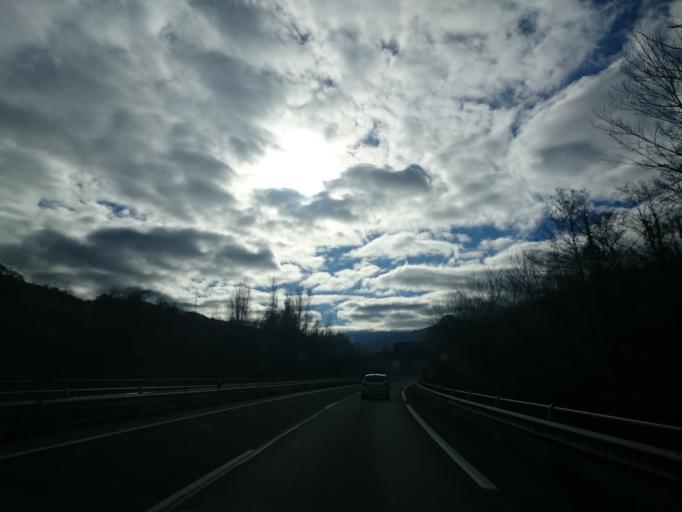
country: ES
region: Asturias
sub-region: Province of Asturias
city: Pola de Lena
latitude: 43.1192
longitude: -5.8160
